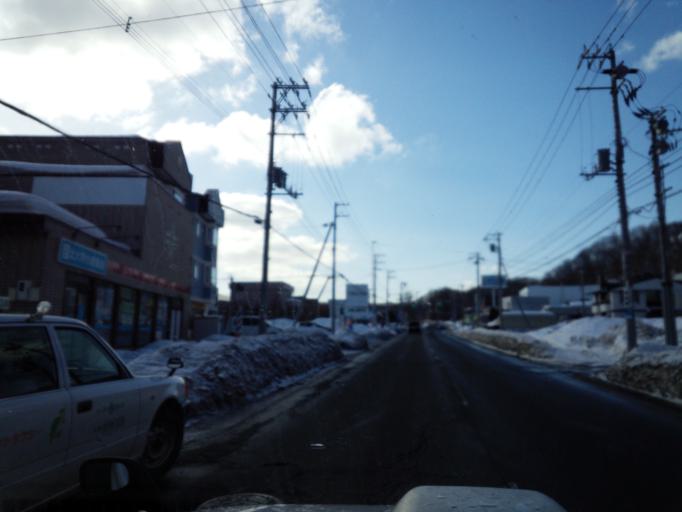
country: JP
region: Hokkaido
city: Sapporo
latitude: 42.9553
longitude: 141.3442
